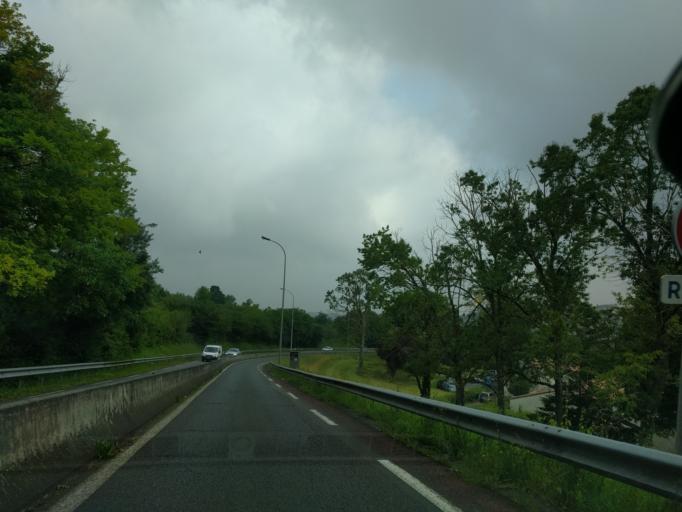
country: FR
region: Poitou-Charentes
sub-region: Departement de la Charente
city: Angouleme
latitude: 45.6392
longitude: 0.1449
